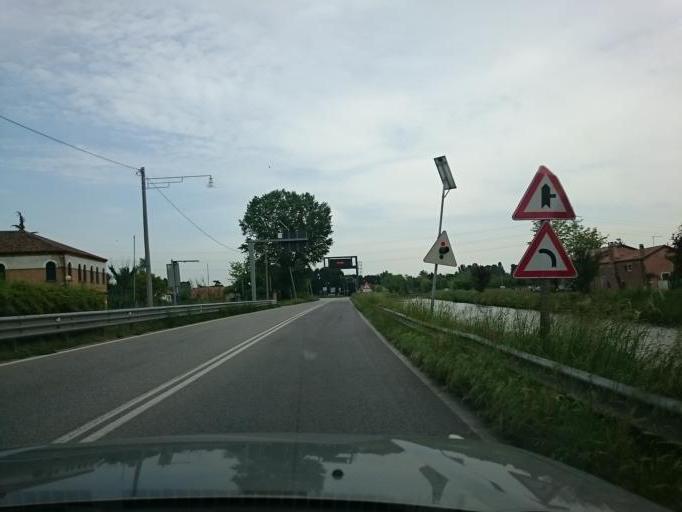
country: IT
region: Veneto
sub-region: Provincia di Venezia
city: Fornase
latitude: 45.4493
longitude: 12.1896
